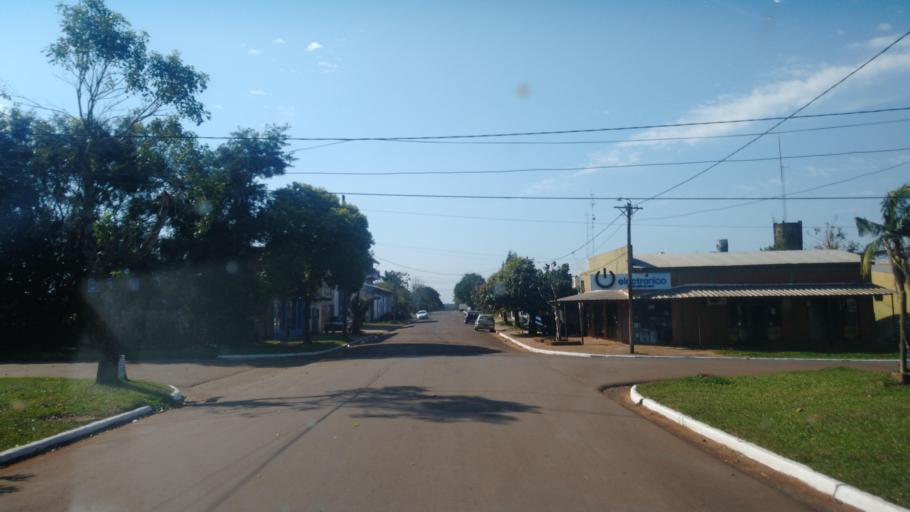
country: AR
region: Misiones
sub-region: Departamento de San Ignacio
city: San Ignacio
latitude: -27.2580
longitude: -55.5409
